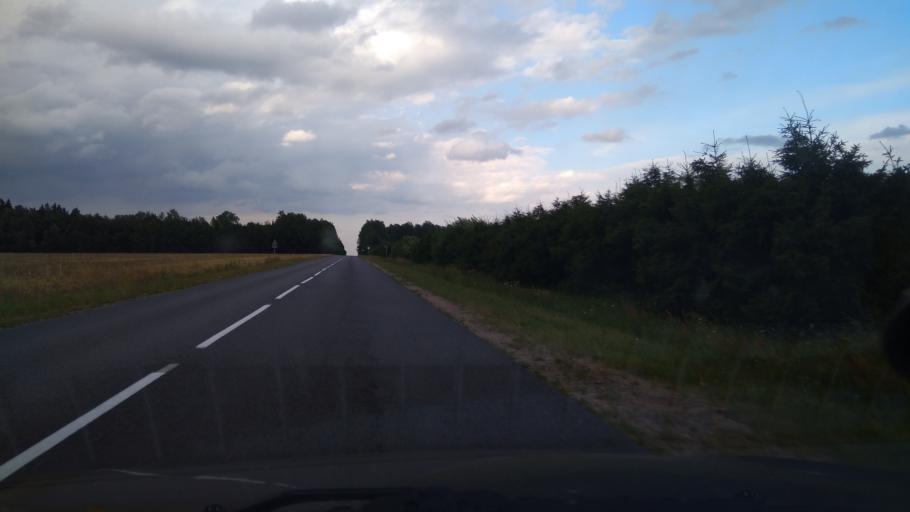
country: BY
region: Minsk
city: Il'ya
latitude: 54.4107
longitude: 27.2527
